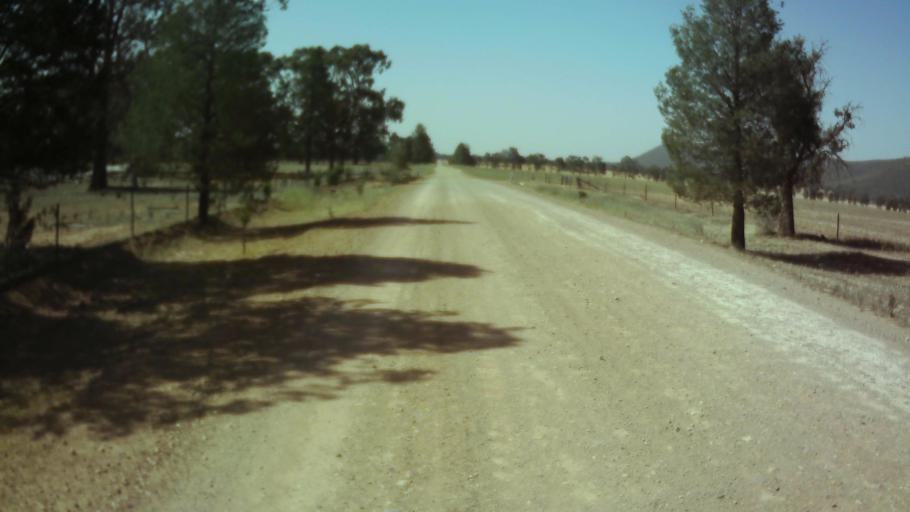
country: AU
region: New South Wales
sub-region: Weddin
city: Grenfell
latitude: -33.9407
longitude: 147.9289
